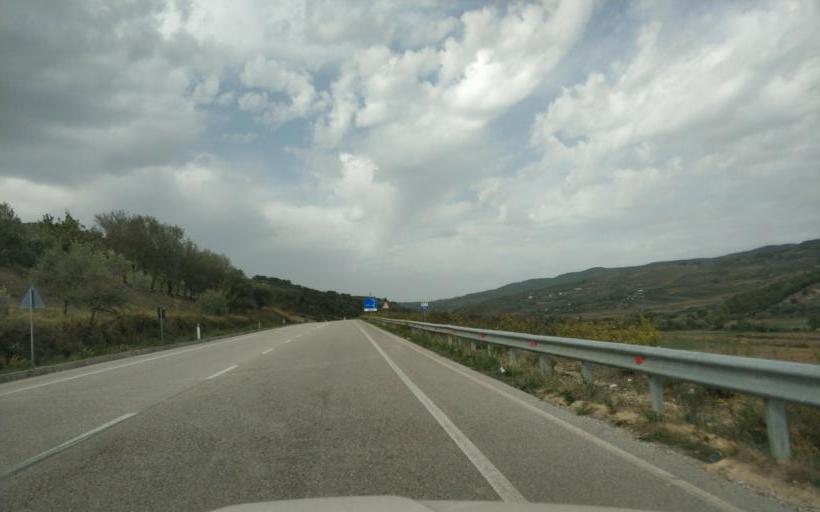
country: AL
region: Gjirokaster
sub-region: Rrethi i Tepelenes
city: Krahes
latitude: 40.4518
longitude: 19.8487
